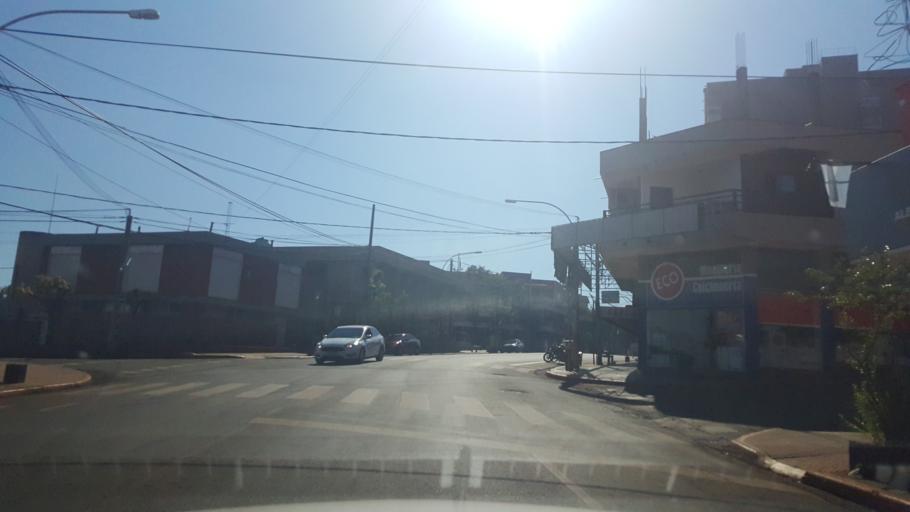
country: AR
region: Misiones
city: Puerto Rico
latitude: -26.8092
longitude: -55.0261
